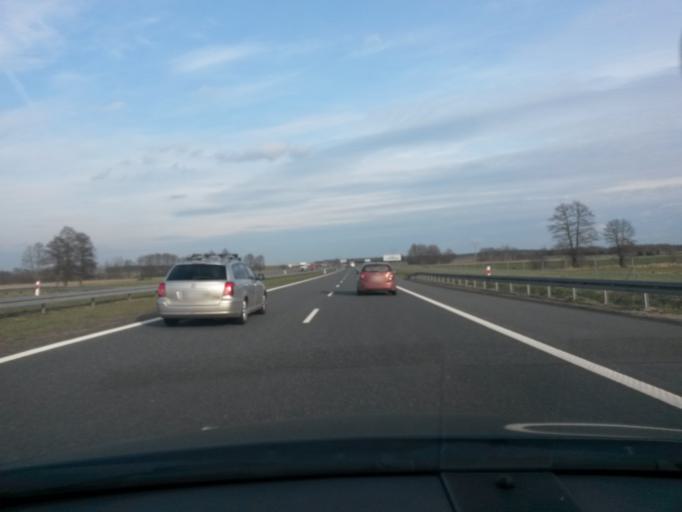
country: PL
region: Lodz Voivodeship
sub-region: Powiat zgierski
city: Ozorkow
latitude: 51.9322
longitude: 19.2800
